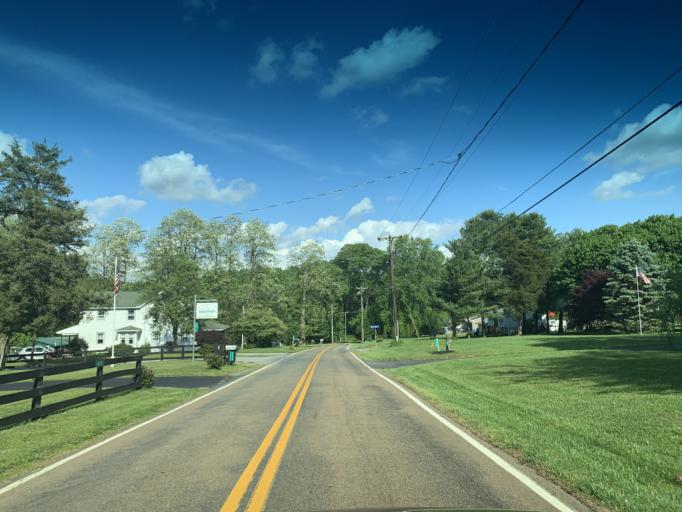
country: US
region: Maryland
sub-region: Cecil County
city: Rising Sun
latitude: 39.6975
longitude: -76.1620
